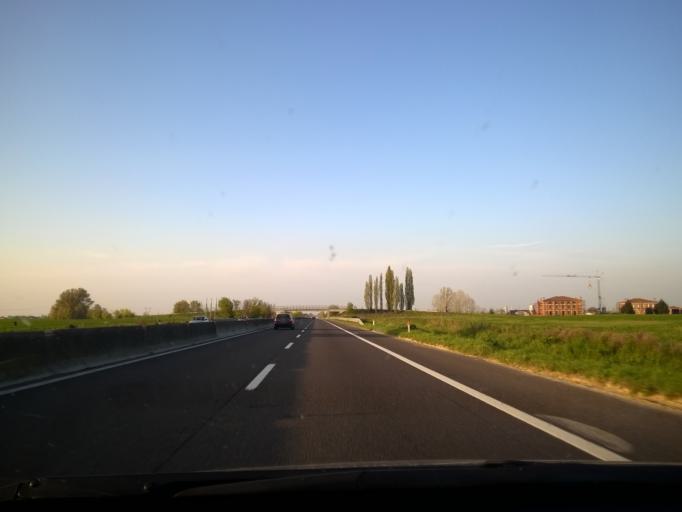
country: IT
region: Emilia-Romagna
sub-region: Provincia di Ferrara
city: Porotto-Cassama
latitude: 44.8186
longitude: 11.5559
